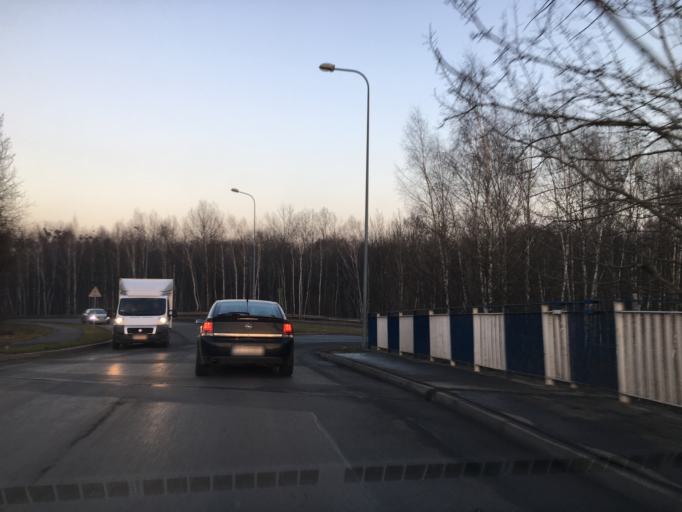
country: PL
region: Silesian Voivodeship
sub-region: Powiat tarnogorski
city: Radzionkow
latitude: 50.3704
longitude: 18.8774
